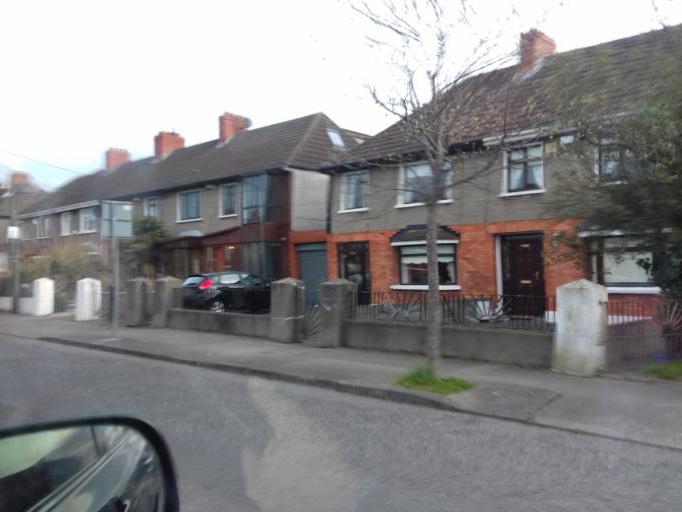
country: IE
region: Leinster
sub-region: Dublin City
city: Finglas
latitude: 53.3934
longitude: -6.2868
